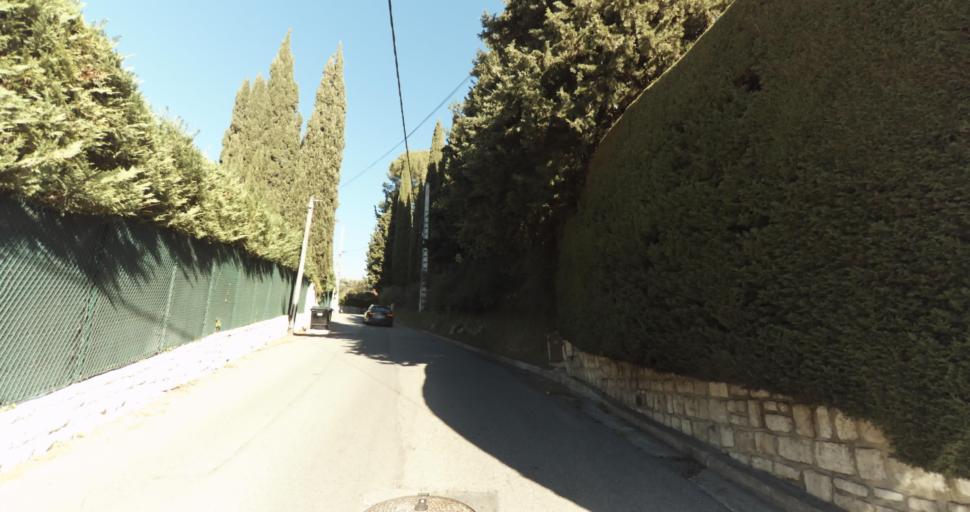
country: FR
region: Provence-Alpes-Cote d'Azur
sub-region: Departement des Alpes-Maritimes
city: Saint-Paul-de-Vence
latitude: 43.7128
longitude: 7.1262
